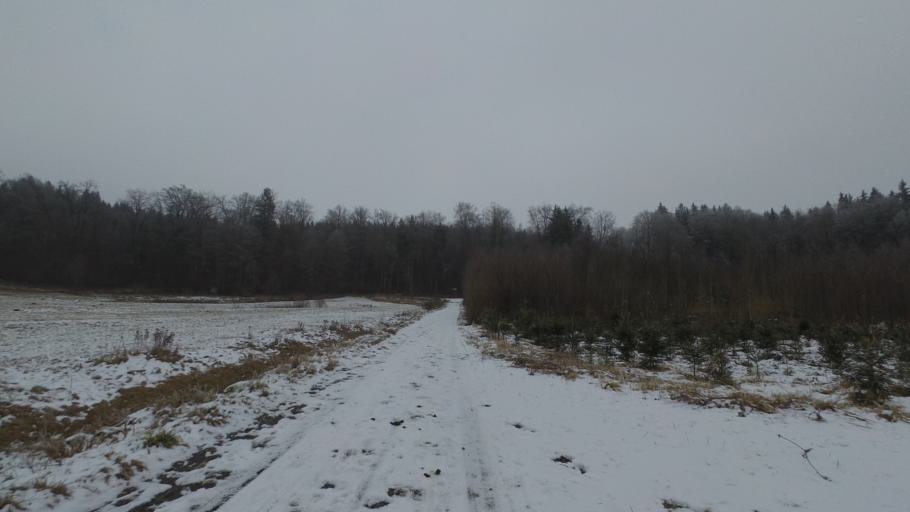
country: DE
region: Bavaria
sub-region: Upper Bavaria
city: Nussdorf
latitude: 47.9016
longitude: 12.5843
